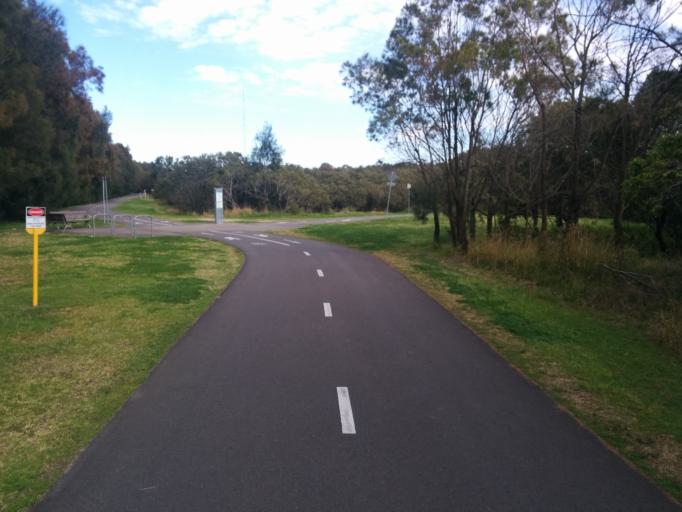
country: AU
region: New South Wales
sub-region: Canada Bay
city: Concord West
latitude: -33.8435
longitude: 151.0825
